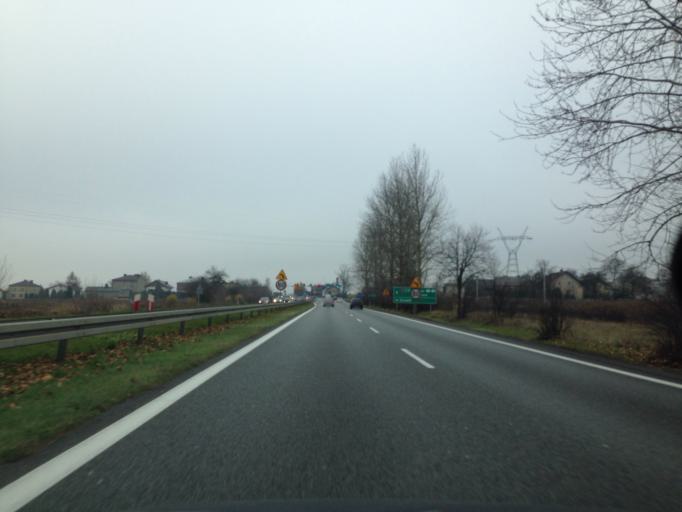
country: PL
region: Silesian Voivodeship
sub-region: Powiat bedzinski
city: Siewierz
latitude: 50.5088
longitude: 19.1963
